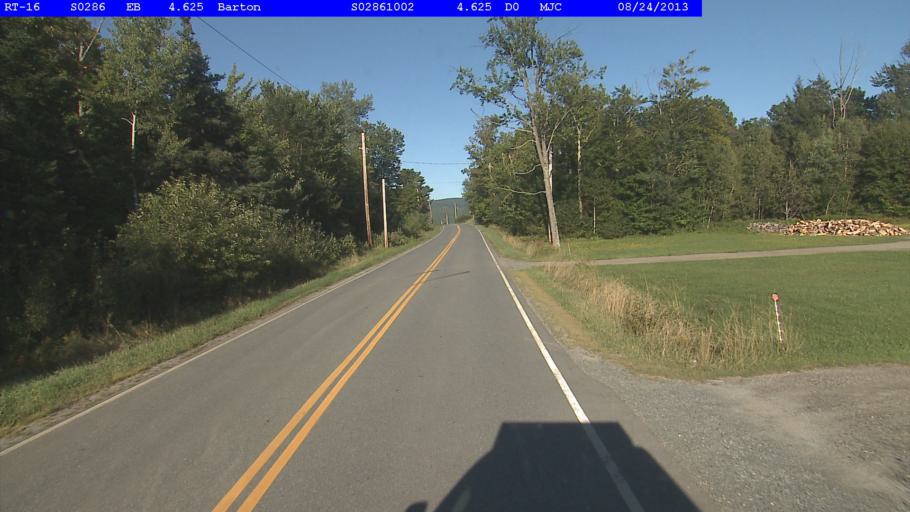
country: US
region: Vermont
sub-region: Orleans County
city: Newport
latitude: 44.7840
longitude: -72.1156
